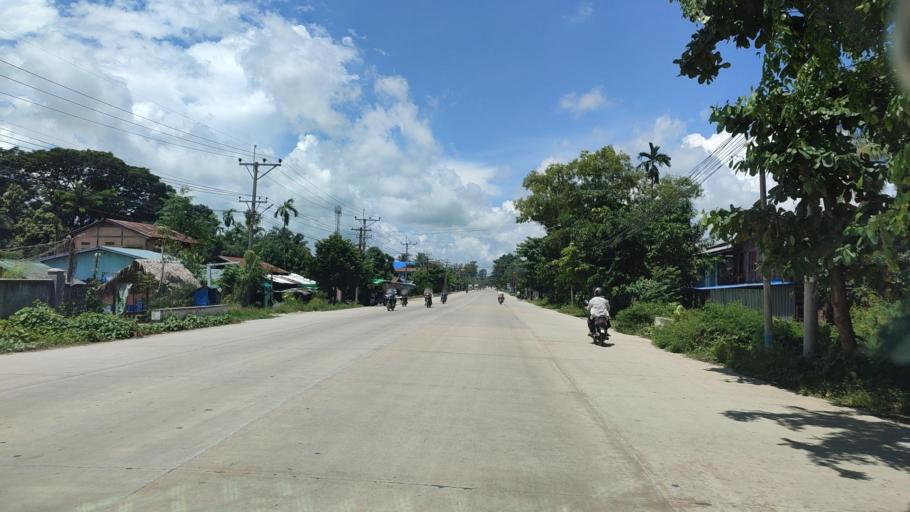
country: MM
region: Bago
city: Taungoo
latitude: 18.9054
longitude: 96.4395
